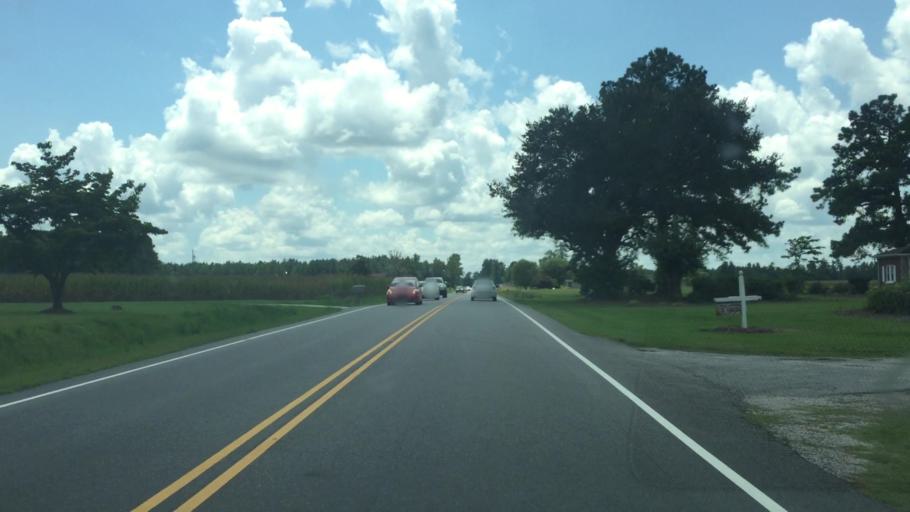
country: US
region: North Carolina
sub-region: Columbus County
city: Tabor City
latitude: 34.2054
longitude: -78.8285
